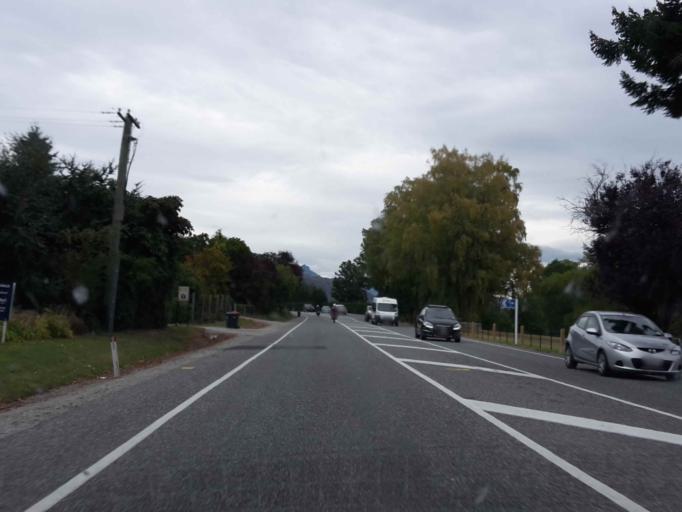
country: NZ
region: Otago
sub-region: Queenstown-Lakes District
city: Arrowtown
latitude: -44.9905
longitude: 168.8097
